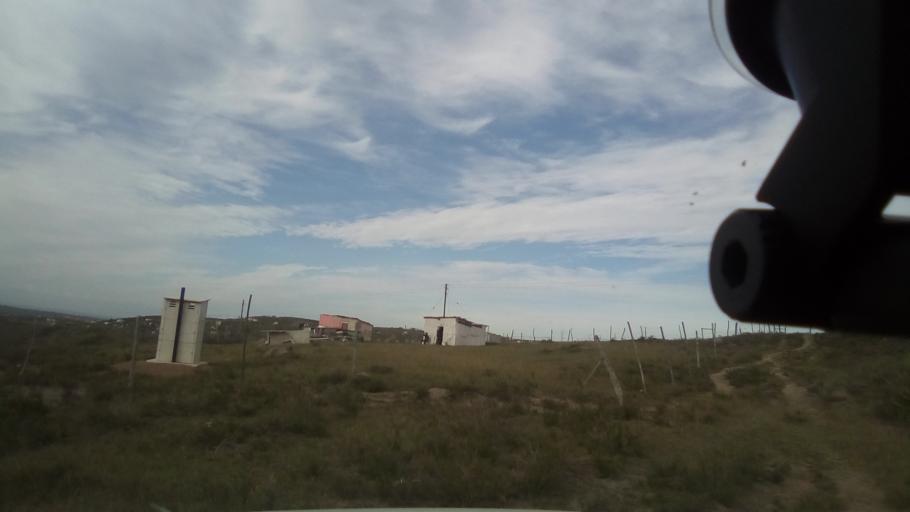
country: ZA
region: Eastern Cape
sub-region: Buffalo City Metropolitan Municipality
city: East London
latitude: -32.7993
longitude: 27.9650
